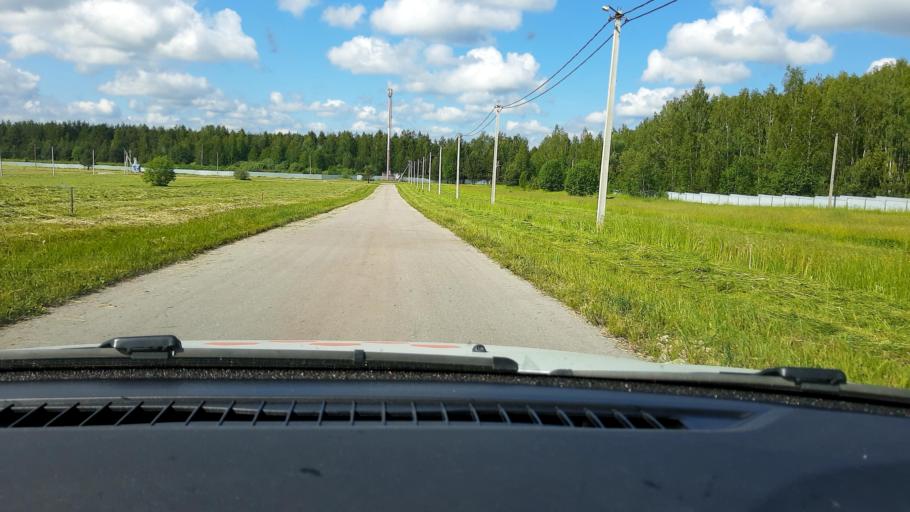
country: RU
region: Nizjnij Novgorod
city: Dal'neye Konstantinovo
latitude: 55.9275
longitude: 43.9873
